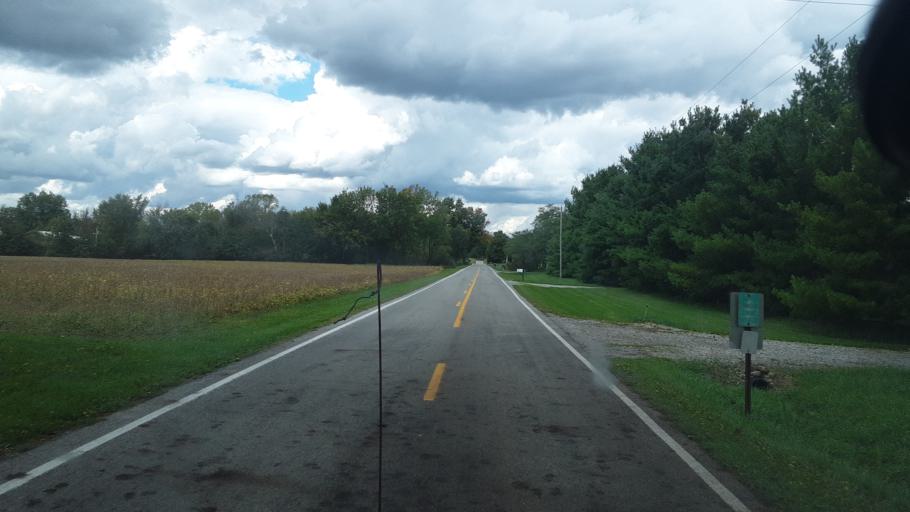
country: US
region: Ohio
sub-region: Knox County
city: Centerburg
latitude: 40.2769
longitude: -82.7507
